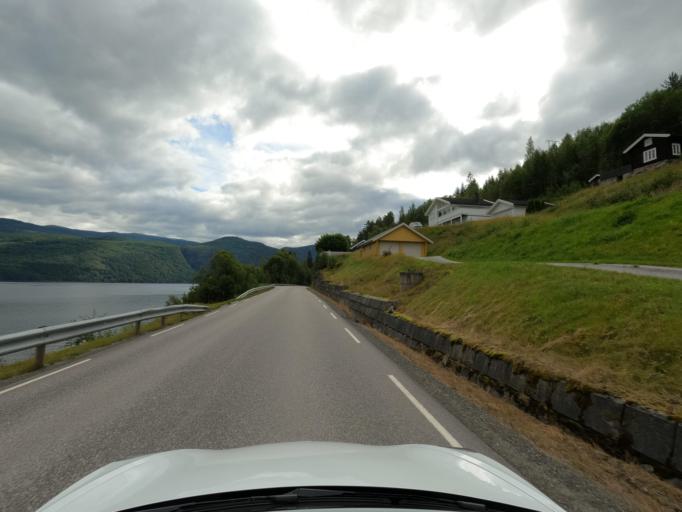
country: NO
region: Telemark
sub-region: Tinn
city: Rjukan
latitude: 59.9734
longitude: 8.7928
